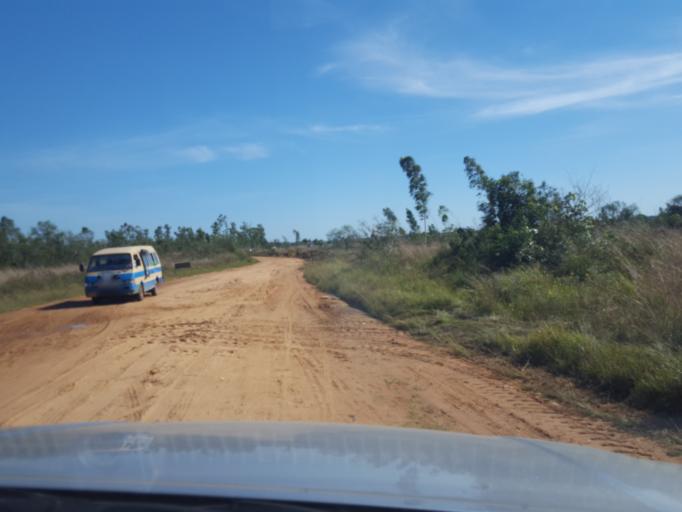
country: PY
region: Cordillera
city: Tobati
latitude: -25.2528
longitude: -57.1103
